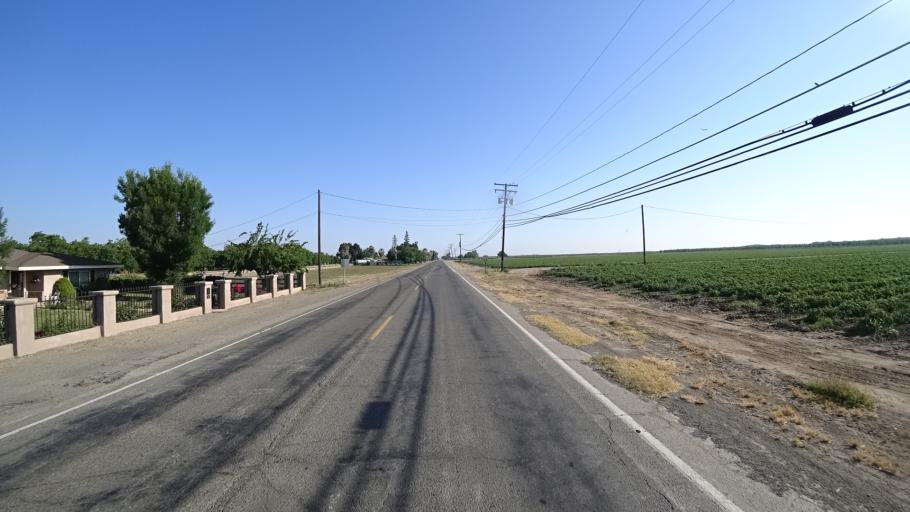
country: US
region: California
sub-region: Kings County
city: Armona
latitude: 36.3502
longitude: -119.7090
